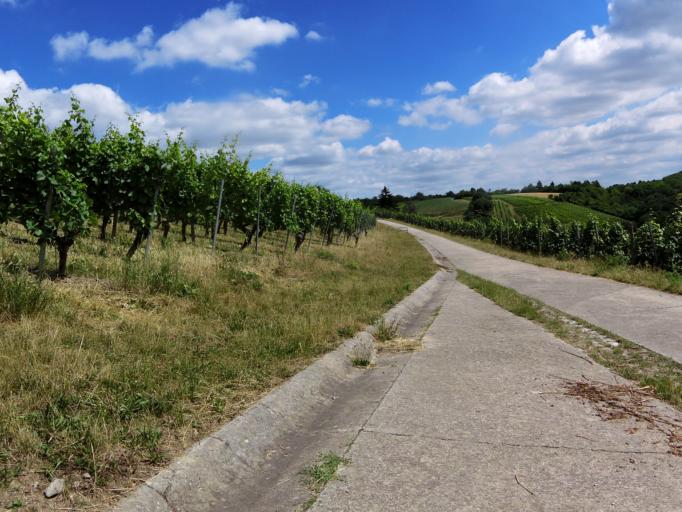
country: DE
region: Bavaria
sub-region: Regierungsbezirk Unterfranken
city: Wuerzburg
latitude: 49.7711
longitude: 9.9596
